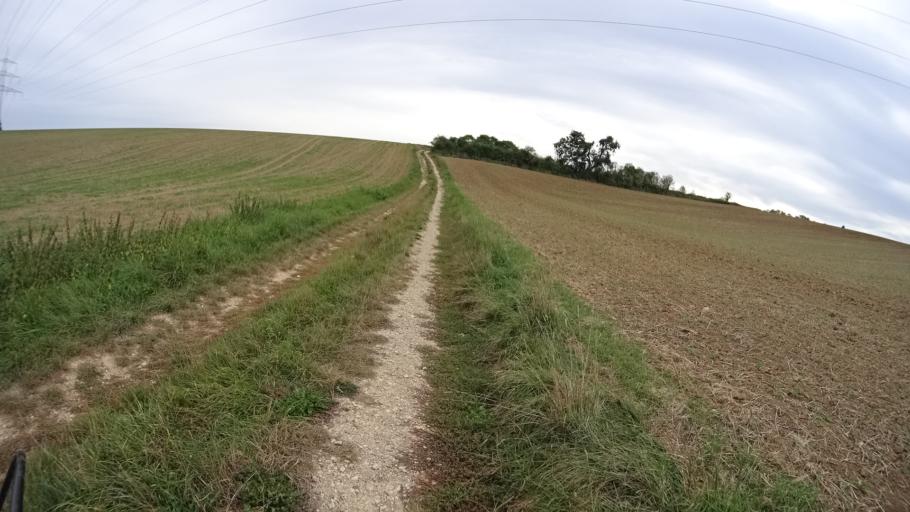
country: DE
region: Bavaria
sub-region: Upper Bavaria
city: Hitzhofen
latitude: 48.8656
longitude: 11.3371
